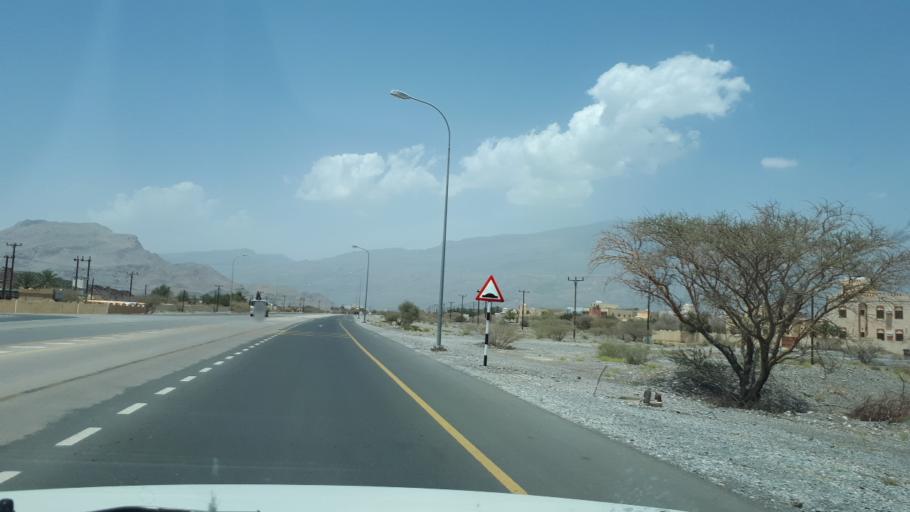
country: OM
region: Muhafazat ad Dakhiliyah
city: Bahla'
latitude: 23.0712
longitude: 57.2735
